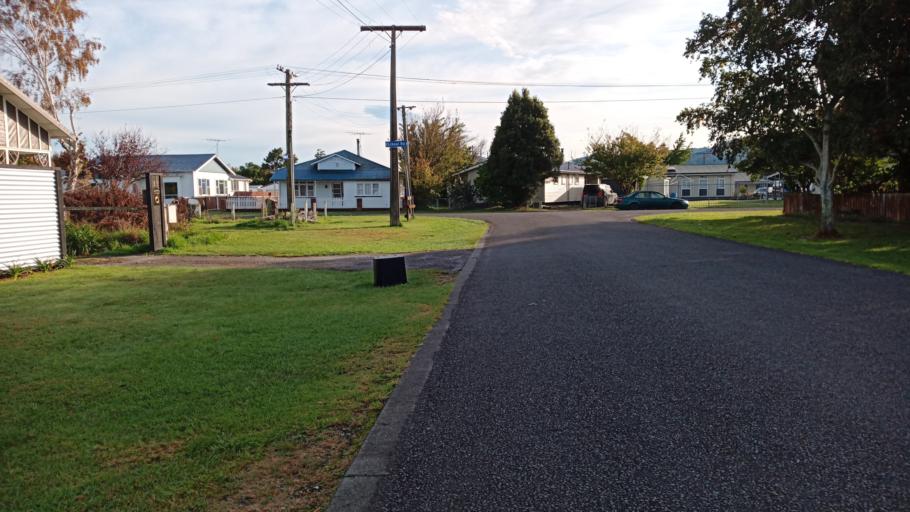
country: NZ
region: Gisborne
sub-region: Gisborne District
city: Gisborne
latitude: -38.6583
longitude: 178.0061
